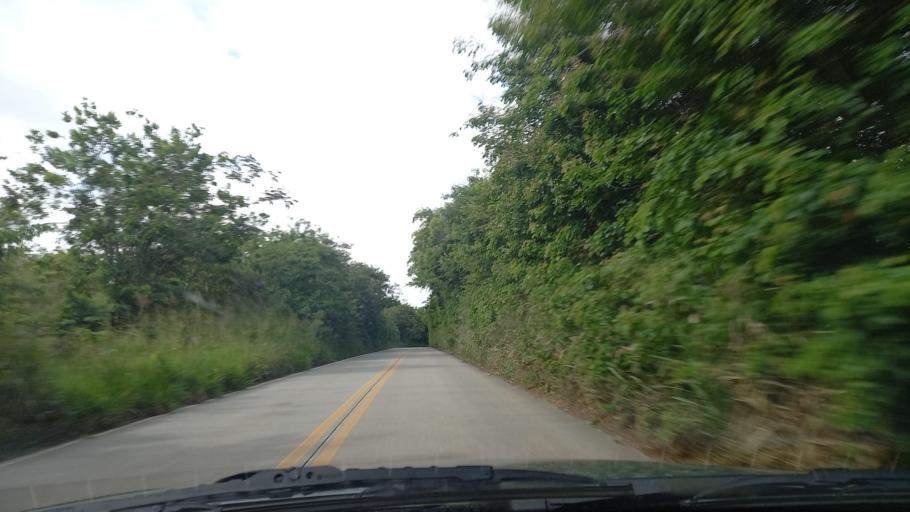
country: BR
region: Pernambuco
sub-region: Quipapa
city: Quipapa
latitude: -8.7849
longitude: -35.9554
